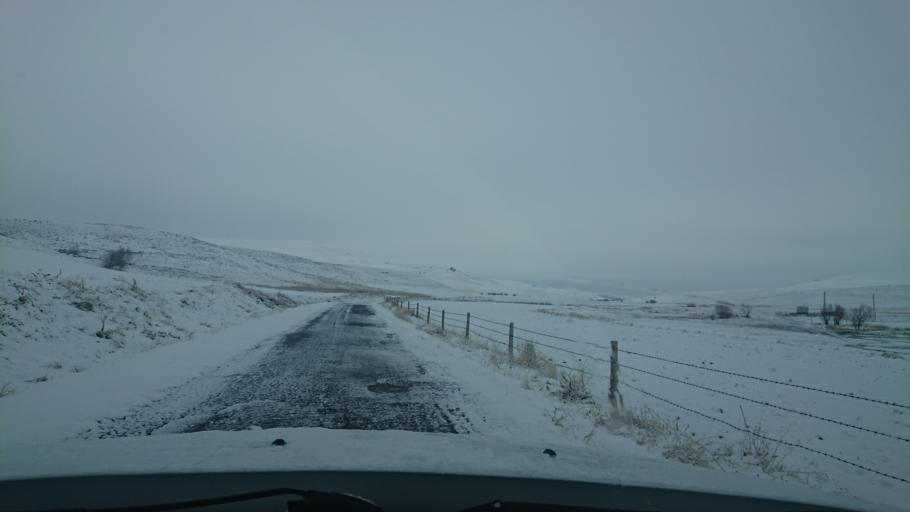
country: TR
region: Aksaray
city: Acipinar
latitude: 38.6806
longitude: 33.8646
